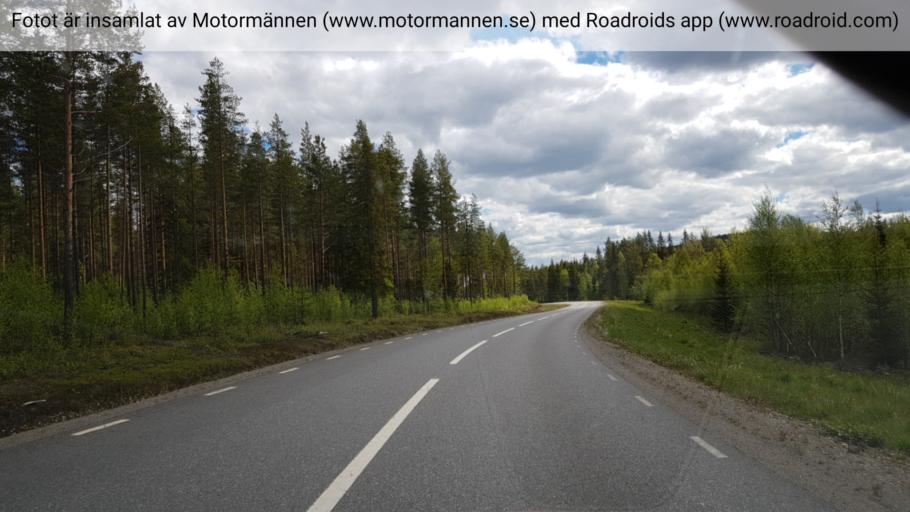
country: SE
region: Vaesterbotten
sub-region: Skelleftea Kommun
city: Langsele
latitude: 64.8402
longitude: 19.8805
